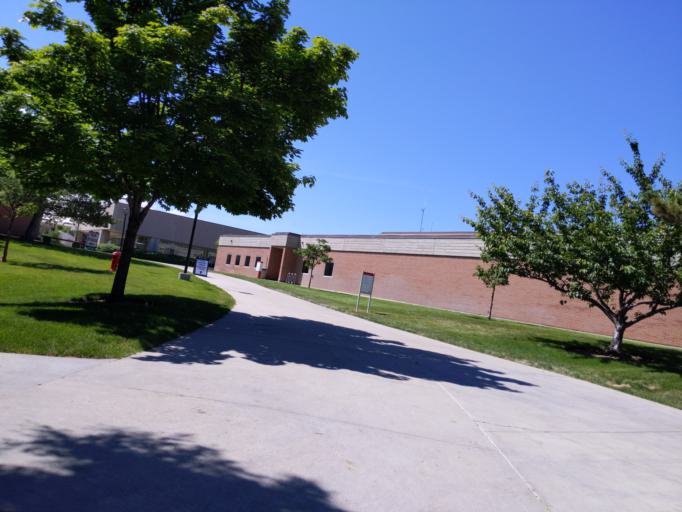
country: US
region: Utah
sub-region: Salt Lake County
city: Salt Lake City
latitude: 40.7644
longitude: -111.8401
